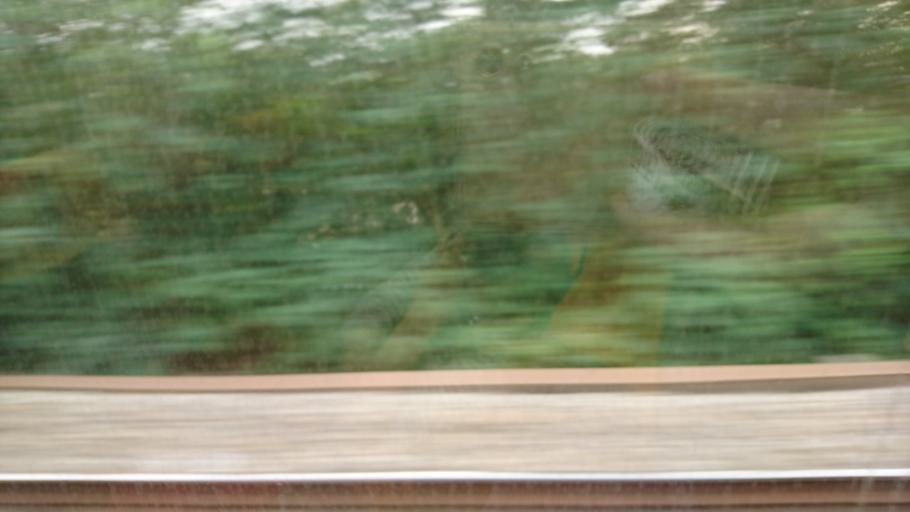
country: TW
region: Taiwan
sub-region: Hsinchu
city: Zhubei
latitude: 24.8579
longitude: 121.0013
